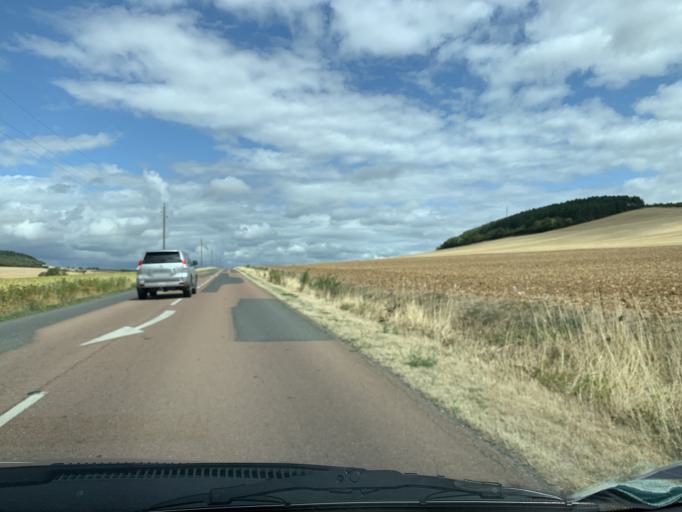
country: FR
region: Bourgogne
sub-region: Departement de la Nievre
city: Varzy
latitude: 47.3654
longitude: 3.4108
